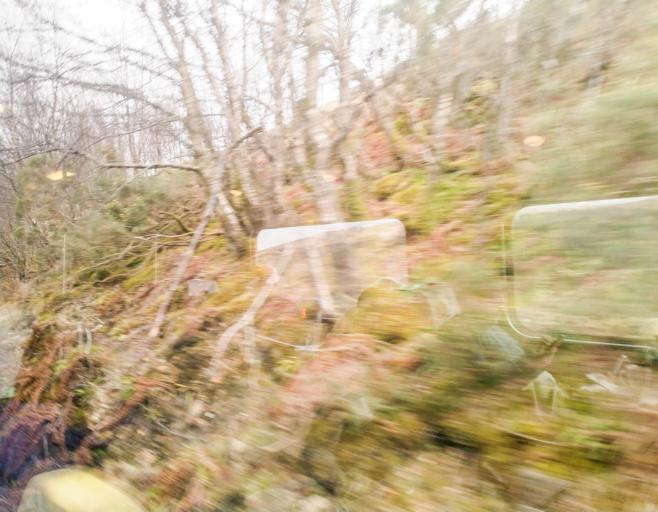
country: GB
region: Scotland
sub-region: Argyll and Bute
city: Garelochhead
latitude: 56.4694
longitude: -4.7172
